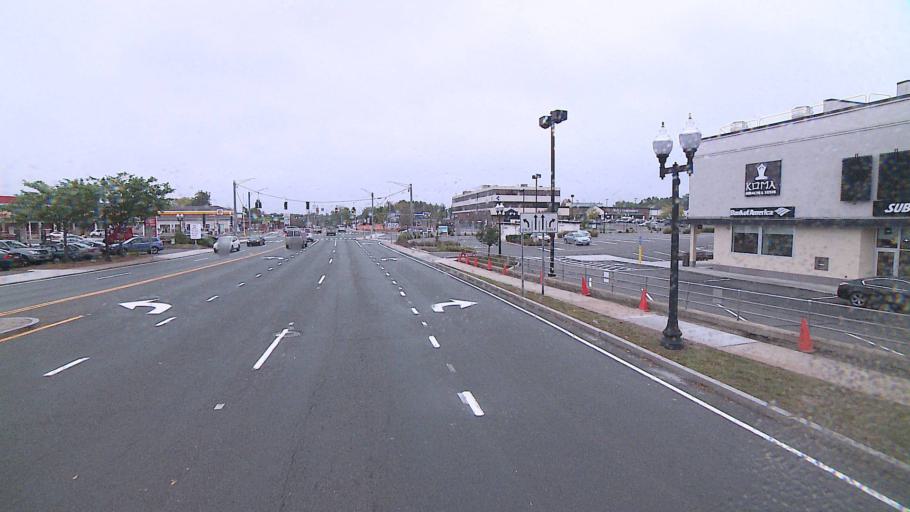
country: US
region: Connecticut
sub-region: Hartford County
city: West Hartford
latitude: 41.7856
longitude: -72.7484
